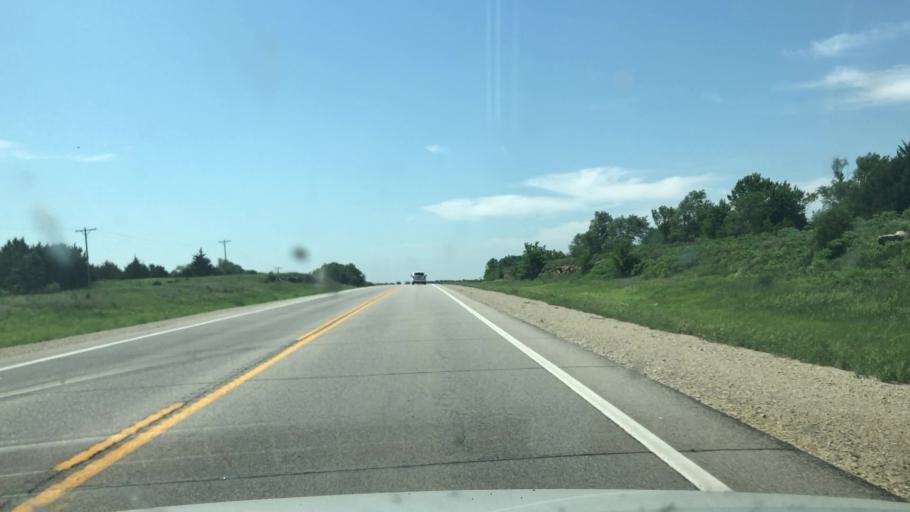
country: US
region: Kansas
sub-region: Cowley County
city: Winfield
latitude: 37.3710
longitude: -97.0071
